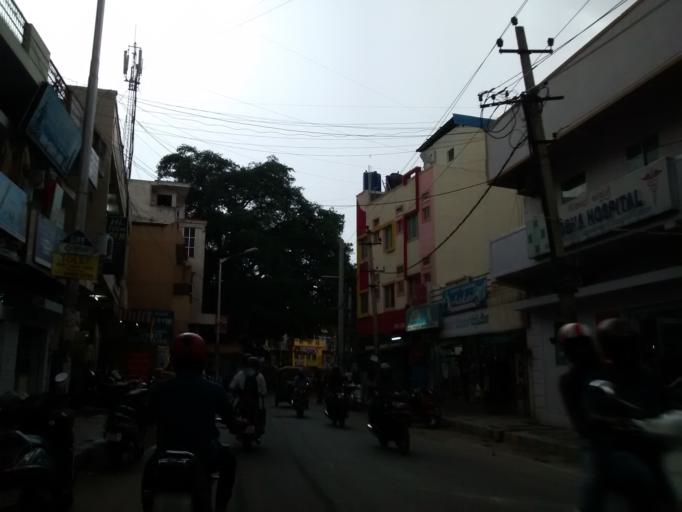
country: IN
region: Karnataka
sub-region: Bangalore Urban
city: Bangalore
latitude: 12.9217
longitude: 77.6110
